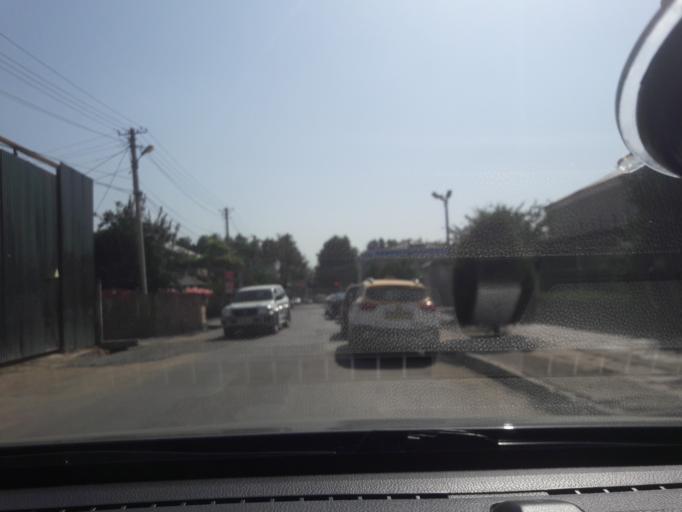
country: TJ
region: Dushanbe
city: Dushanbe
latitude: 38.5644
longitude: 68.8047
